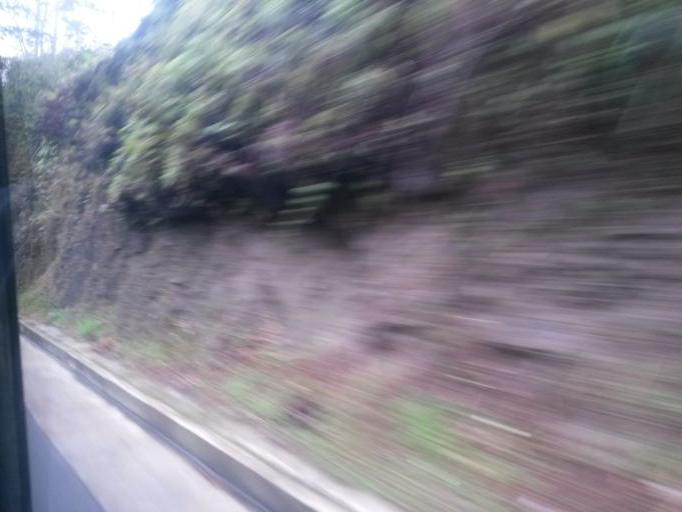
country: CO
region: Cauca
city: Popayan
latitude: 2.4244
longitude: -76.6254
